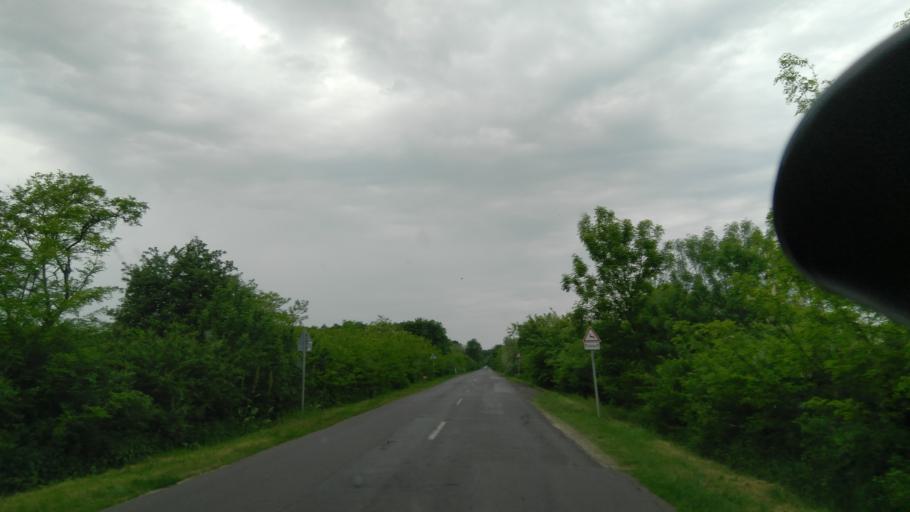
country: HU
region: Bekes
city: Doboz
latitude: 46.7221
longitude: 21.3076
